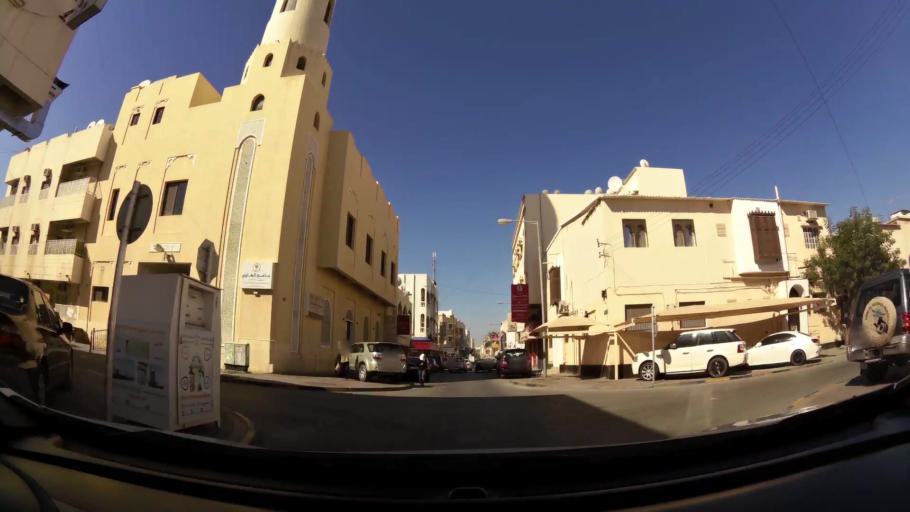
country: BH
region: Muharraq
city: Al Muharraq
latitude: 26.2611
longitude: 50.6131
